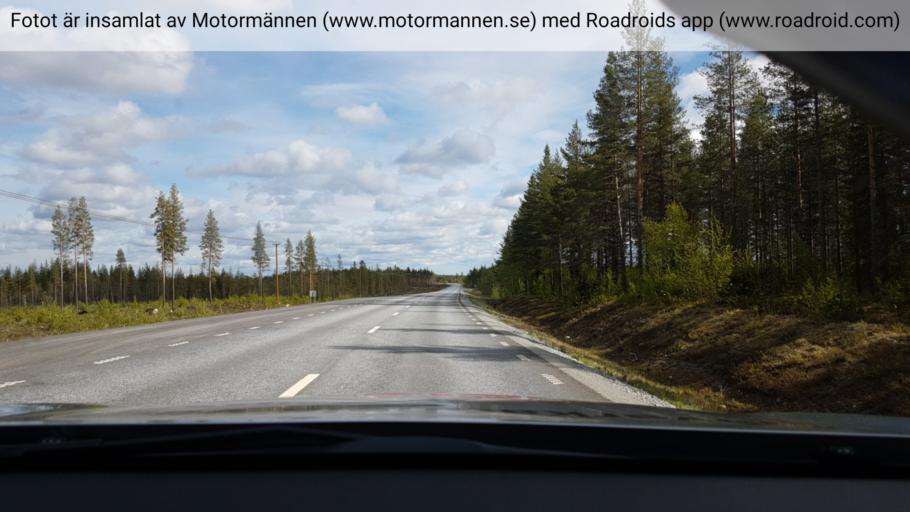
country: SE
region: Vaesterbotten
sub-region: Asele Kommun
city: Insjon
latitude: 64.1254
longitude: 18.0831
